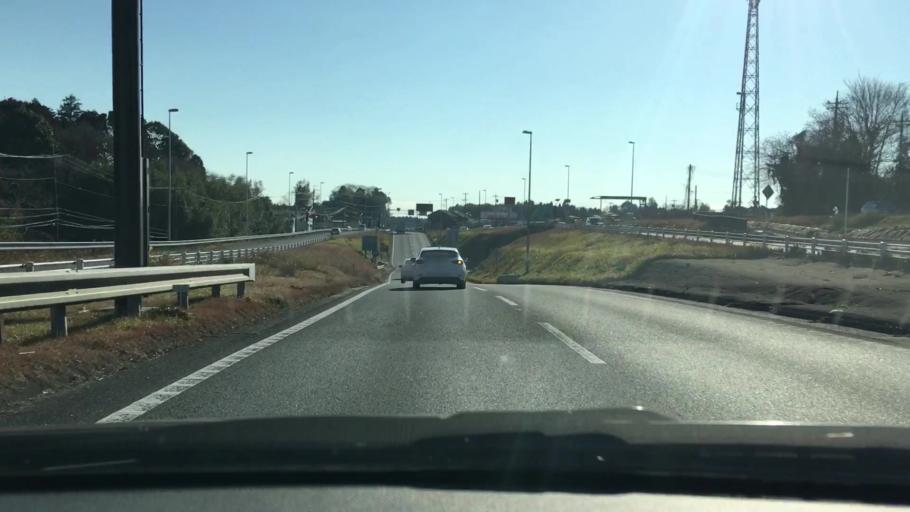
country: JP
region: Chiba
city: Sakura
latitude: 35.6872
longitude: 140.2427
